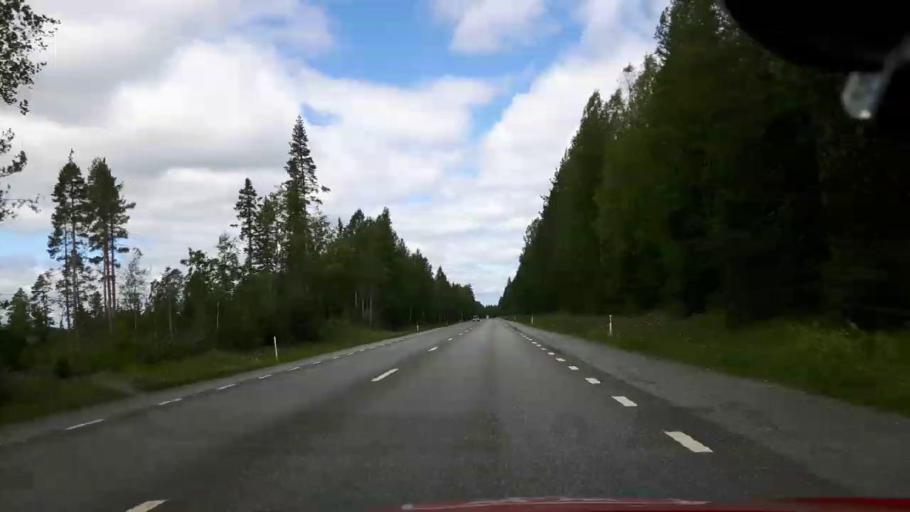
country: SE
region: Jaemtland
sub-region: Braecke Kommun
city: Braecke
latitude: 62.7217
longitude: 15.4490
